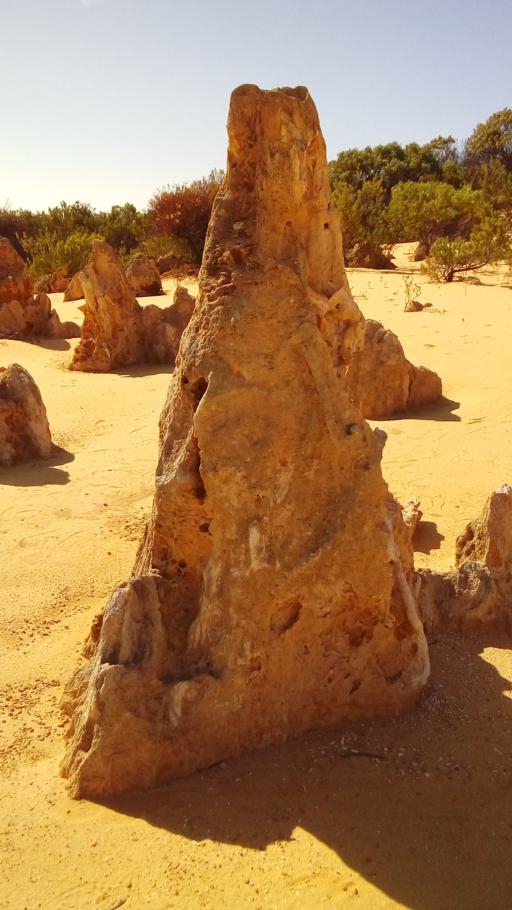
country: AU
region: Western Australia
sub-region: Dandaragan
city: Jurien Bay
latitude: -30.6031
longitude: 115.1610
